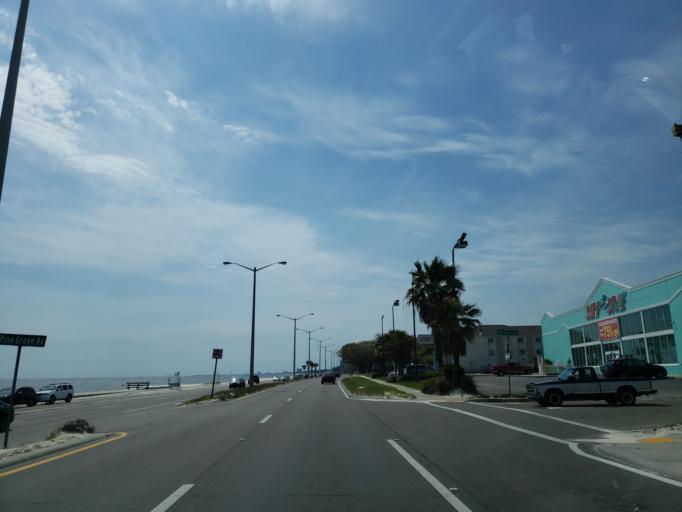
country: US
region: Mississippi
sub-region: Harrison County
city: Biloxi
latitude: 30.3905
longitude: -88.9808
